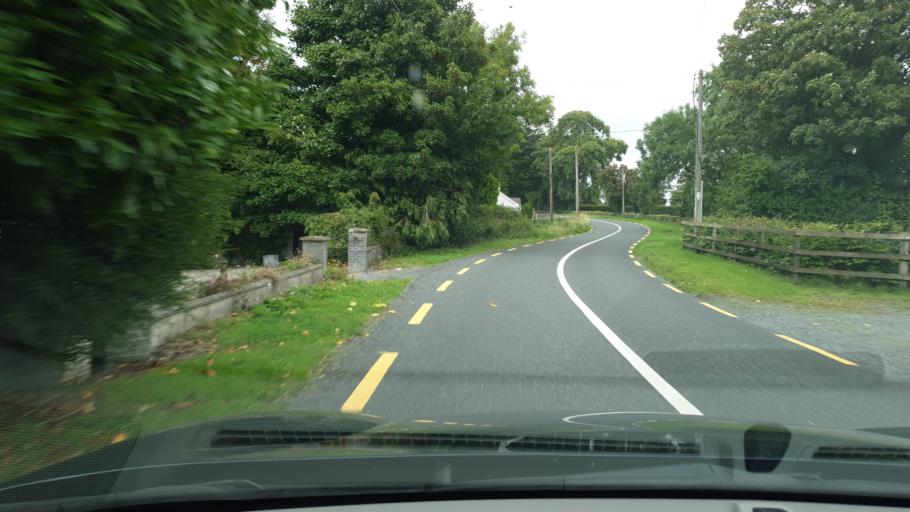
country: IE
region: Leinster
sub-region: Kildare
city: Naas
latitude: 53.2309
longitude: -6.6975
